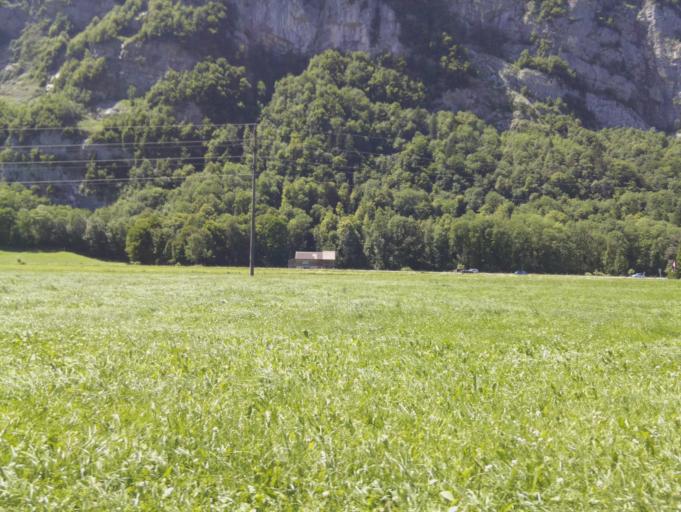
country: CH
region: Glarus
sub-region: Glarus
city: Nafels
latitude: 47.0826
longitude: 9.0574
